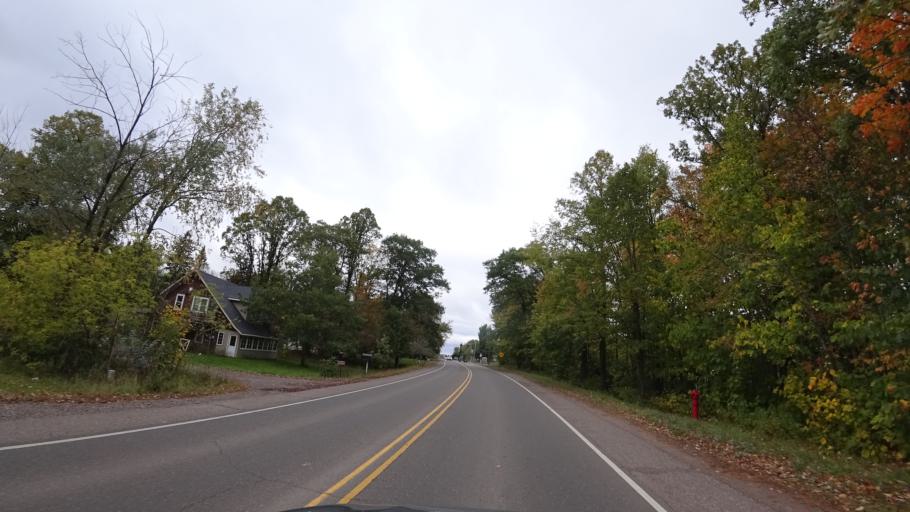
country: US
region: Wisconsin
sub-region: Rusk County
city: Ladysmith
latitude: 45.4718
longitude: -91.1108
